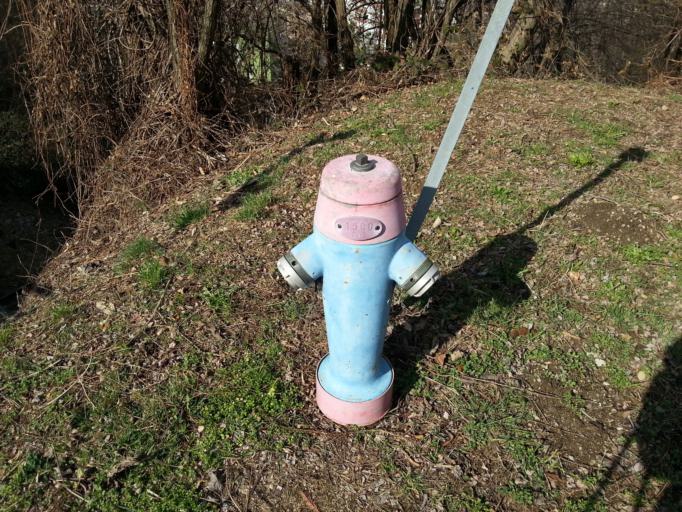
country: CH
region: Ticino
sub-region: Lugano District
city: Sorengo
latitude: 45.9863
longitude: 8.9458
